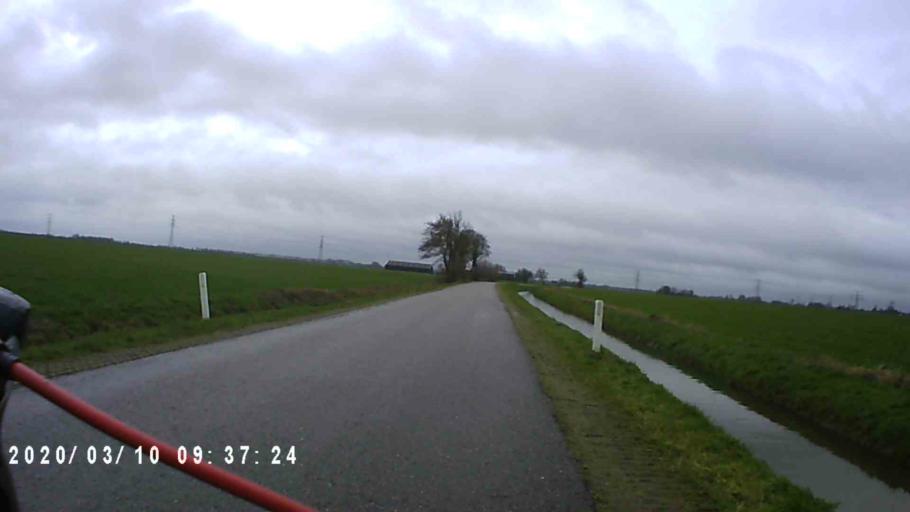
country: NL
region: Groningen
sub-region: Gemeente Winsum
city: Winsum
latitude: 53.2987
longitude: 6.4915
